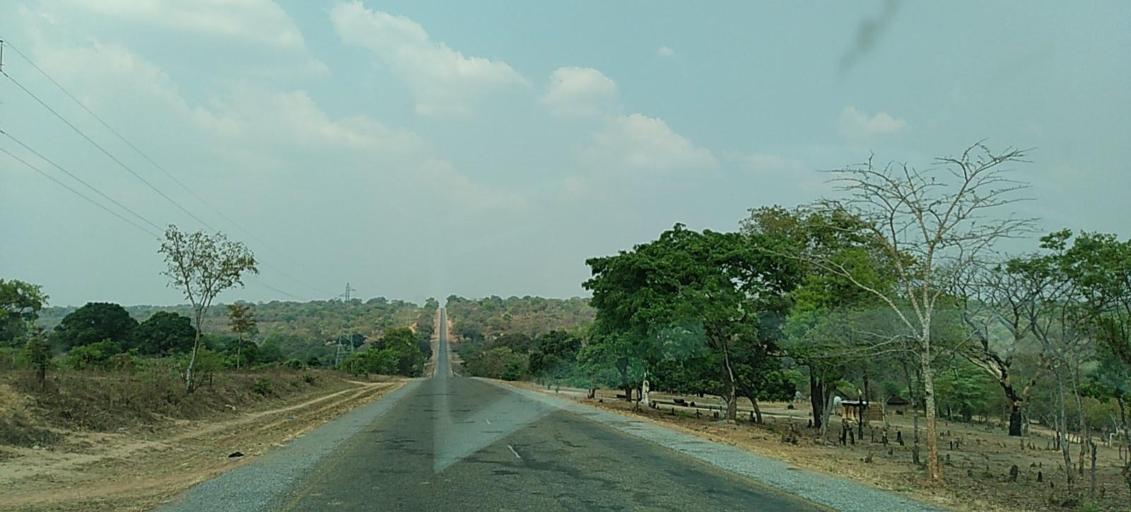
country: ZM
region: North-Western
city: Kabompo
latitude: -13.6212
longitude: 24.1190
